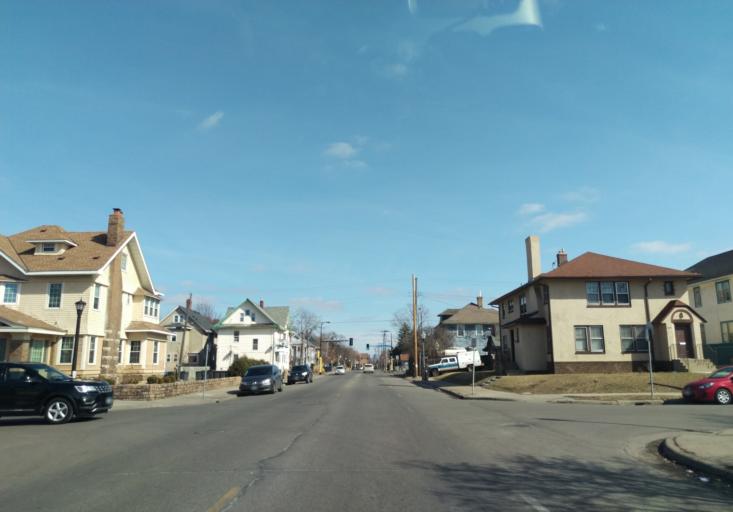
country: US
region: Minnesota
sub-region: Hennepin County
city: Minneapolis
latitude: 44.9466
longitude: -93.2693
